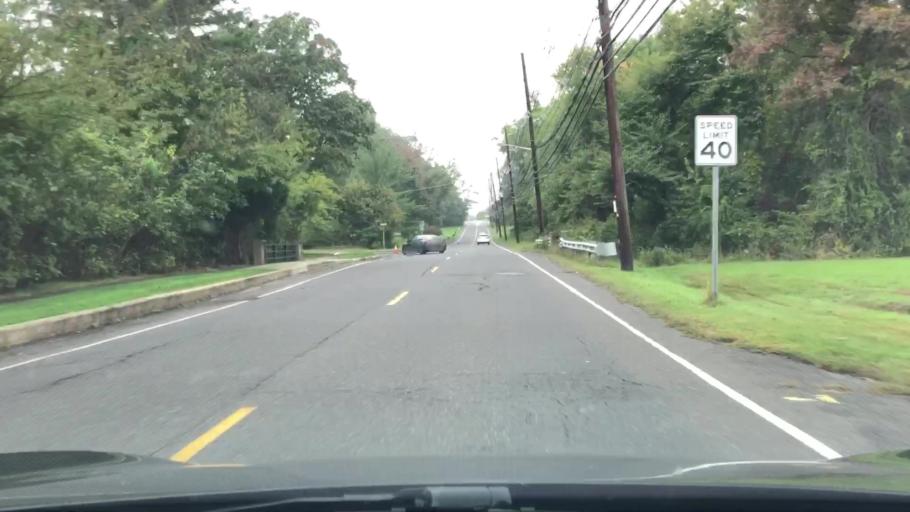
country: US
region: New Jersey
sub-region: Mercer County
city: Ewing
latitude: 40.2879
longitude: -74.7795
